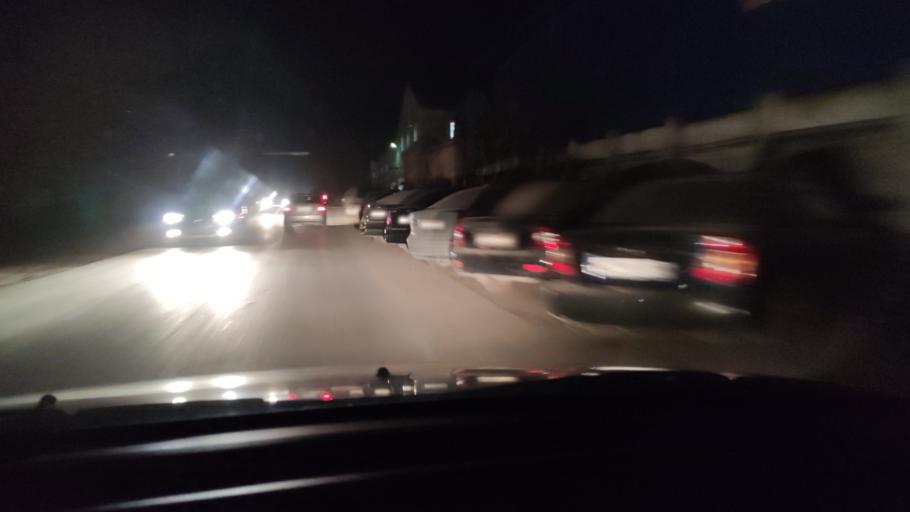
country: RU
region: Perm
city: Froly
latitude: 57.9665
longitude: 56.2720
